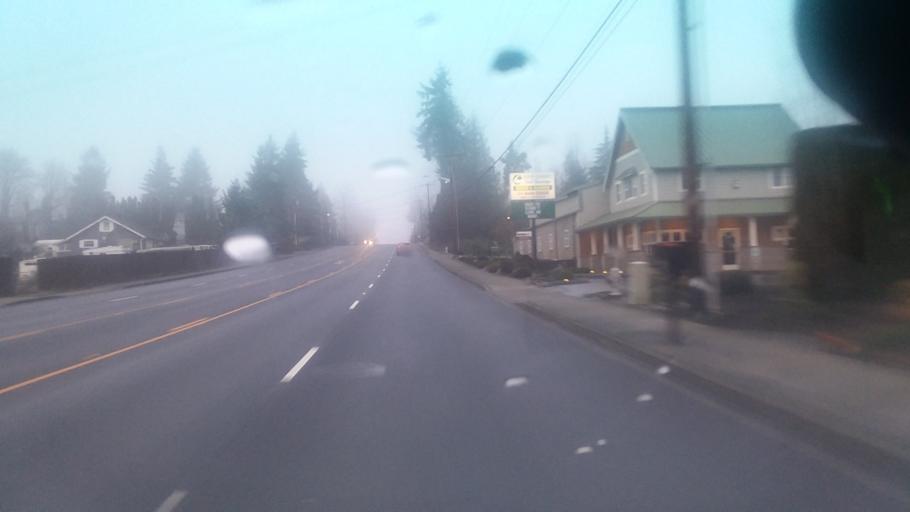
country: US
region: Washington
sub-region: Pierce County
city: Summit
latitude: 47.1549
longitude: -122.3377
